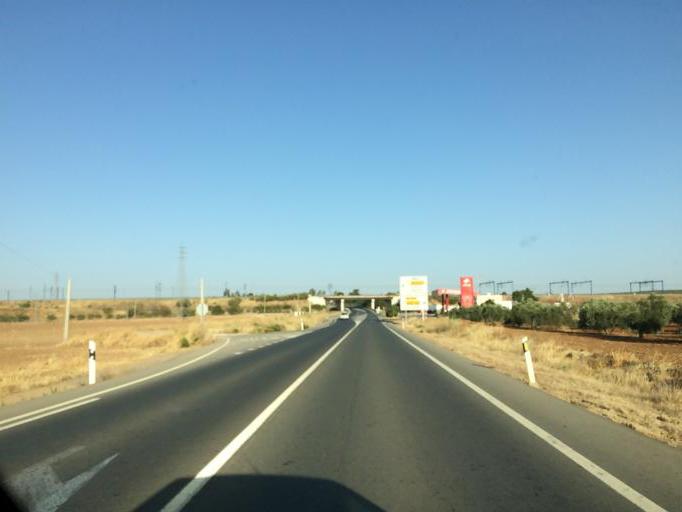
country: ES
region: Andalusia
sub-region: Provincia de Malaga
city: Humilladero
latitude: 37.0621
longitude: -4.7131
